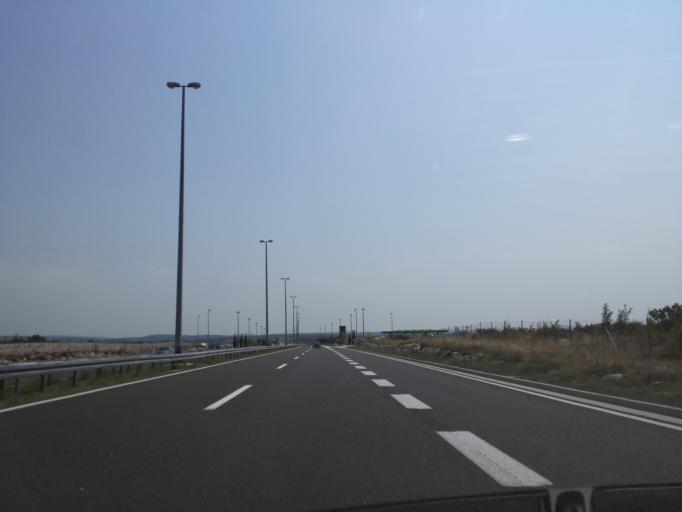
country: HR
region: Zadarska
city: Polaca
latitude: 44.0651
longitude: 15.5265
